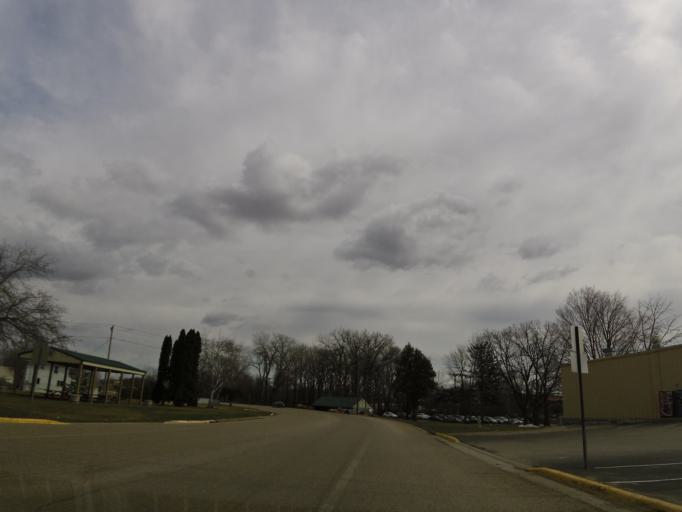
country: US
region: Minnesota
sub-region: Goodhue County
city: Pine Island
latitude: 44.2042
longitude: -92.6459
